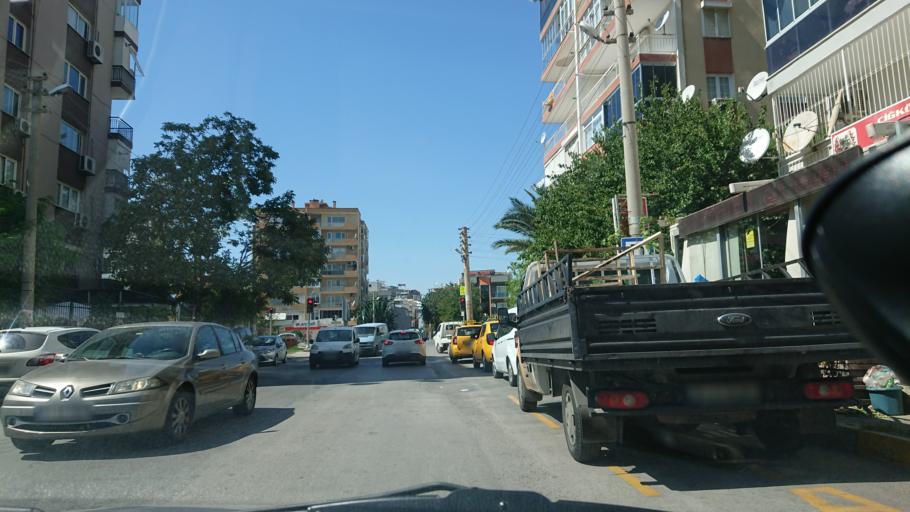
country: TR
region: Izmir
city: Karsiyaka
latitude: 38.4799
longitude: 27.1158
